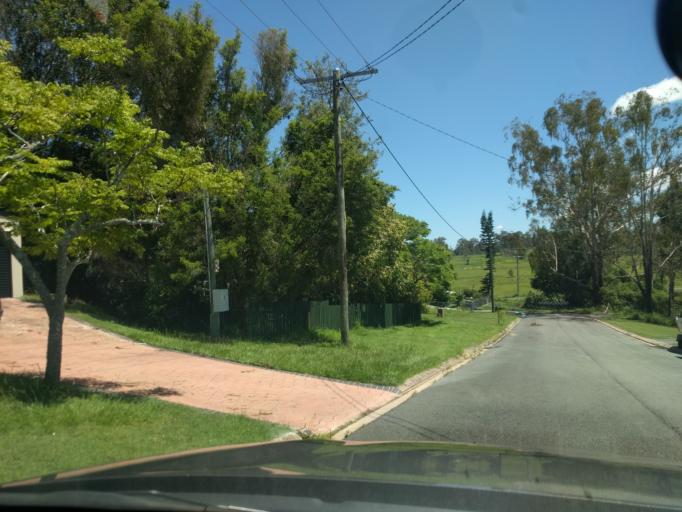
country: AU
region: Queensland
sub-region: Logan
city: Cedar Vale
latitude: -27.9855
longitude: 153.0052
